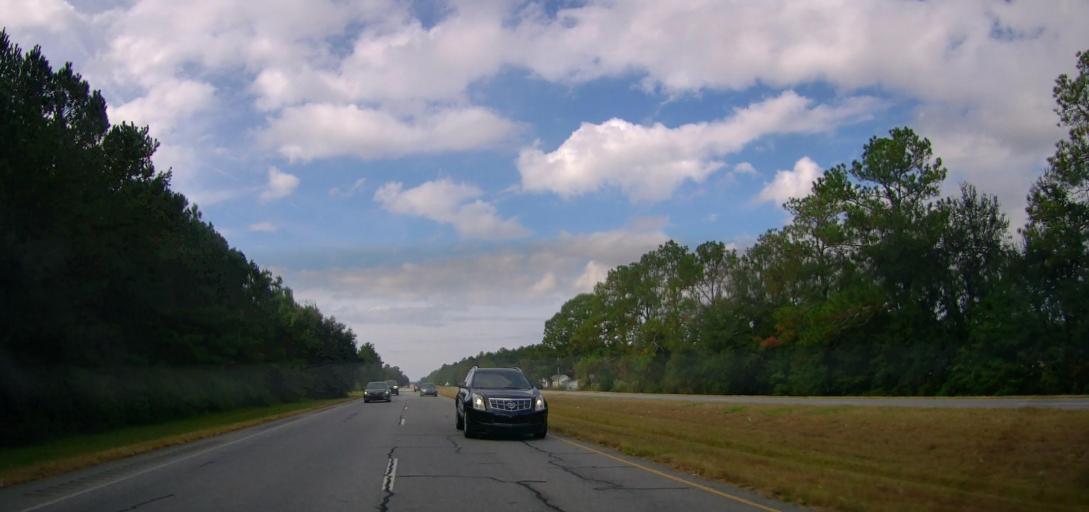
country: US
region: Georgia
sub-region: Mitchell County
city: Pelham
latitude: 31.1841
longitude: -84.1560
